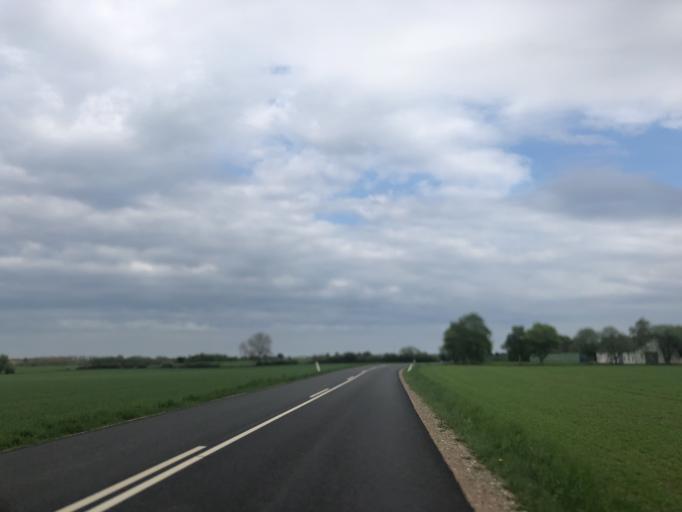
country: DK
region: Zealand
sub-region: Koge Kommune
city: Koge
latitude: 55.4724
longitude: 12.1414
